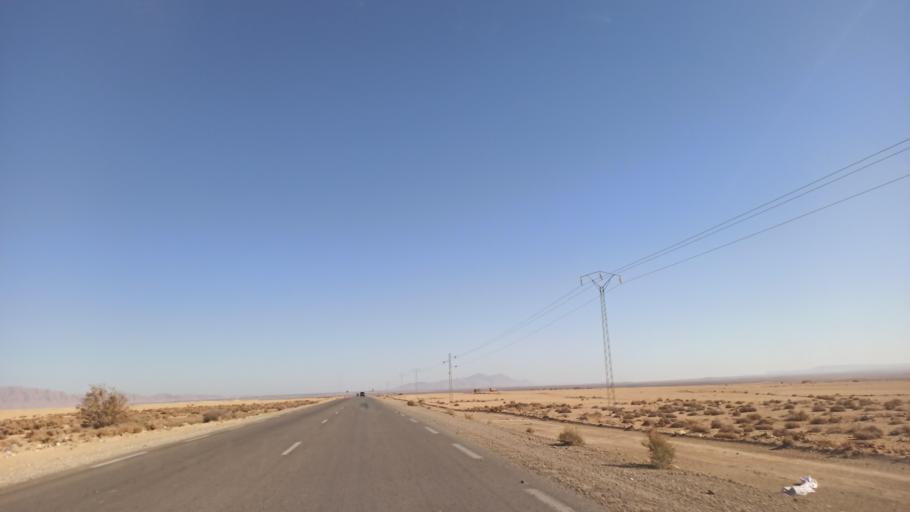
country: TN
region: Gafsa
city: Al Metlaoui
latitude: 34.3239
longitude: 8.5312
